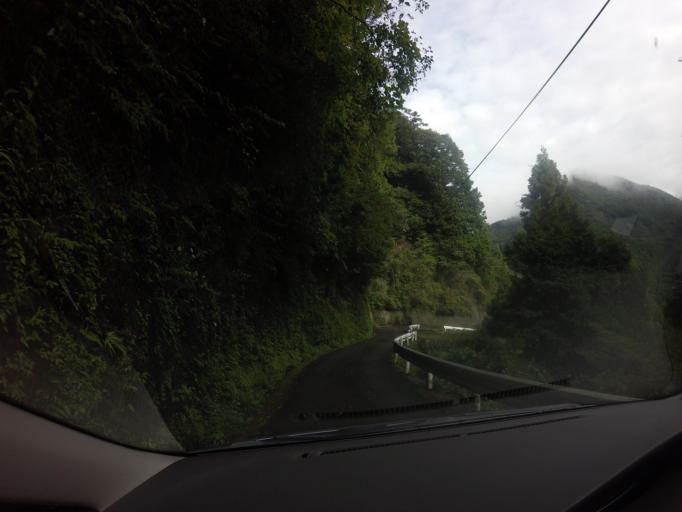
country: JP
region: Wakayama
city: Shingu
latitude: 33.9675
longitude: 135.8094
